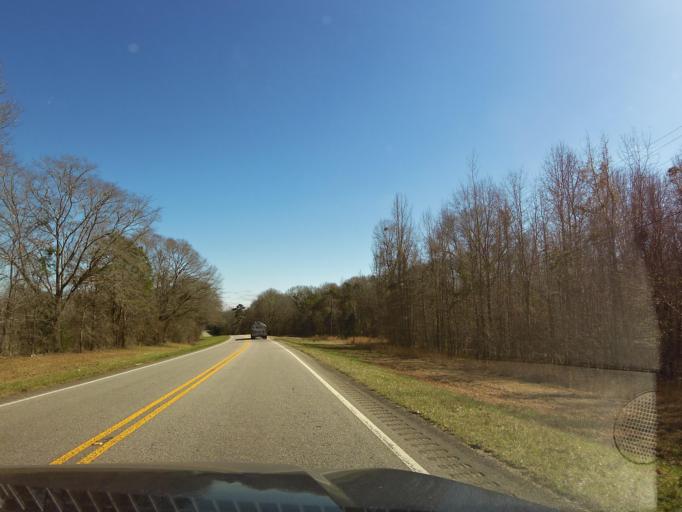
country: US
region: Alabama
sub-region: Bullock County
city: Union Springs
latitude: 32.0880
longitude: -85.5463
